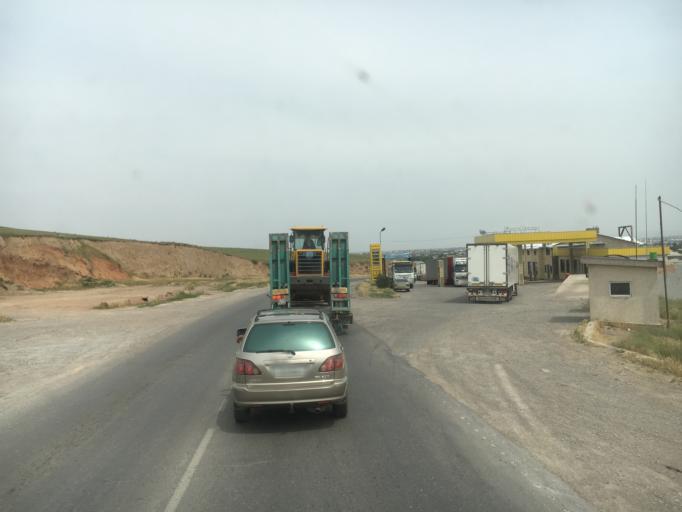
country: KZ
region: Ongtustik Qazaqstan
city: Shymkent
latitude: 42.3275
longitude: 69.5137
